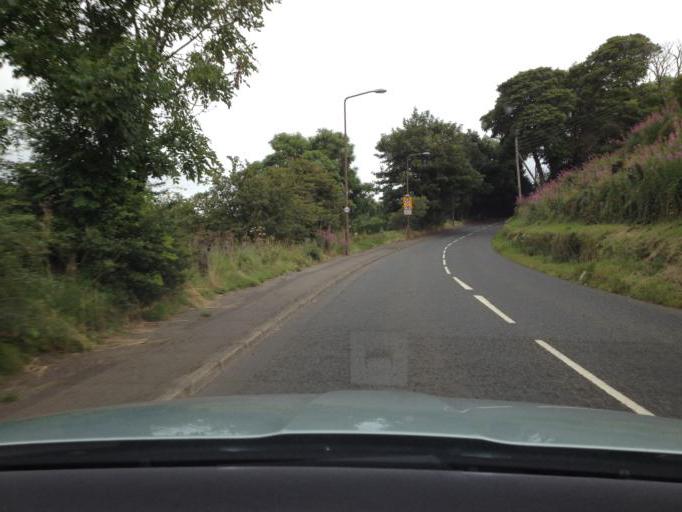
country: GB
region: Scotland
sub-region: West Lothian
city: Bathgate
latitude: 55.9326
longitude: -3.6509
